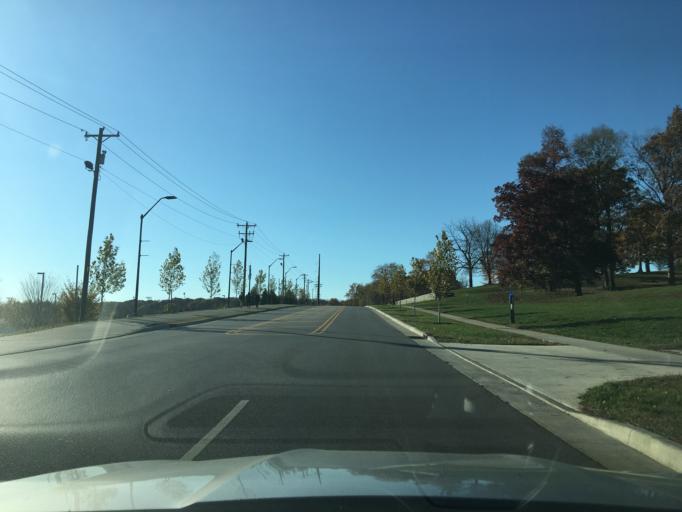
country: US
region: Indiana
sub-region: Tippecanoe County
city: West Lafayette
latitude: 40.4315
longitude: -86.9233
